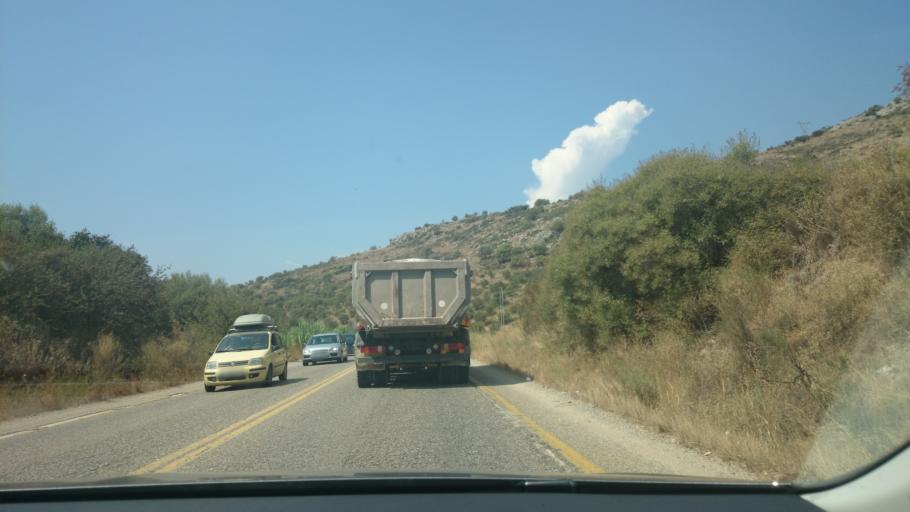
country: GR
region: West Greece
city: Aitoliko
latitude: 38.4118
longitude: 21.3970
